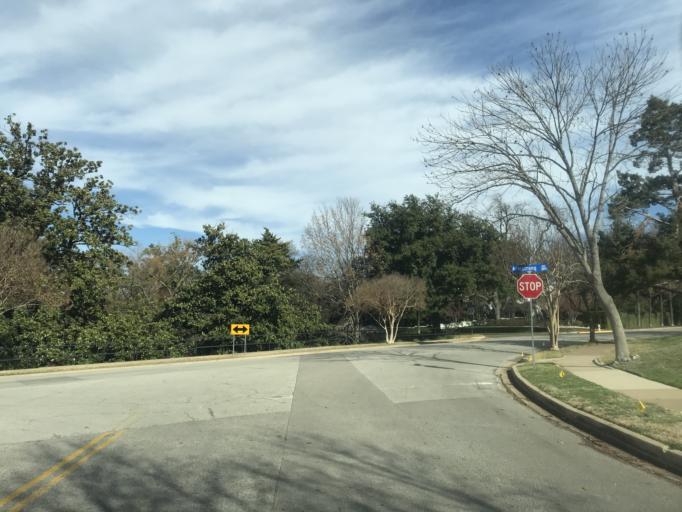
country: US
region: Texas
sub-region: Dallas County
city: Highland Park
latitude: 32.8230
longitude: -96.7988
